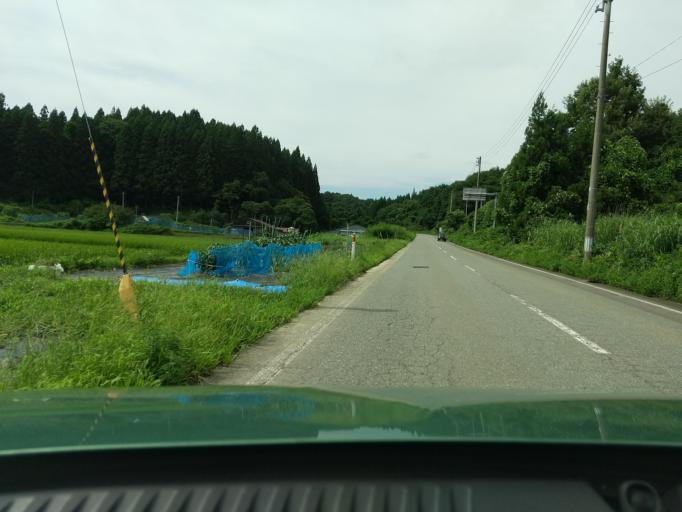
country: JP
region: Akita
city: Akita
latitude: 39.7150
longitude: 140.1924
